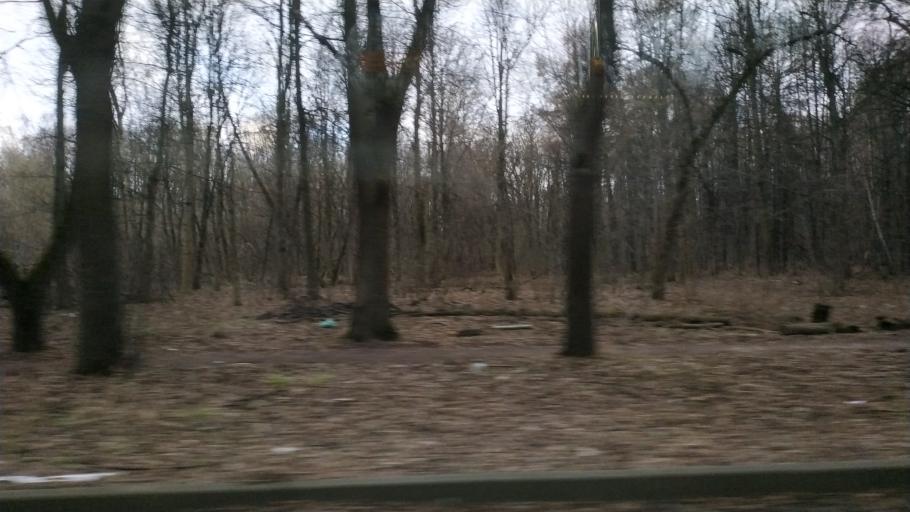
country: RU
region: Moscow
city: Metrogorodok
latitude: 55.7865
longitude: 37.7574
